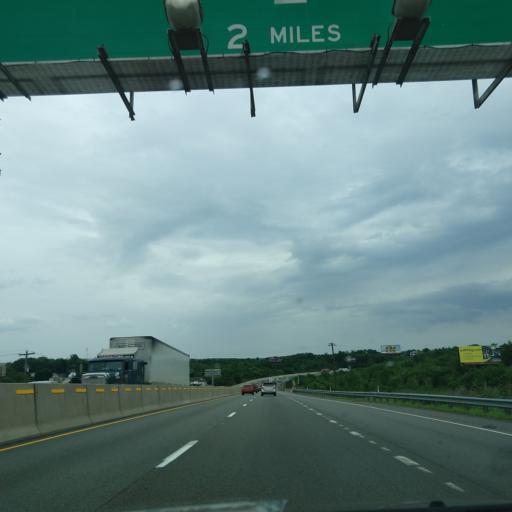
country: US
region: Pennsylvania
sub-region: Lackawanna County
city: Throop
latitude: 41.4486
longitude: -75.6350
